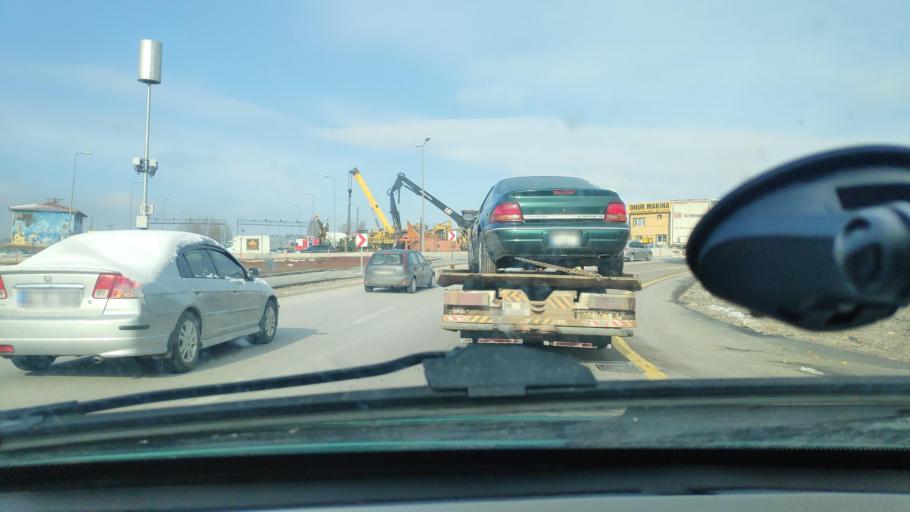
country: TR
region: Ankara
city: Batikent
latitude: 40.0137
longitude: 32.7763
